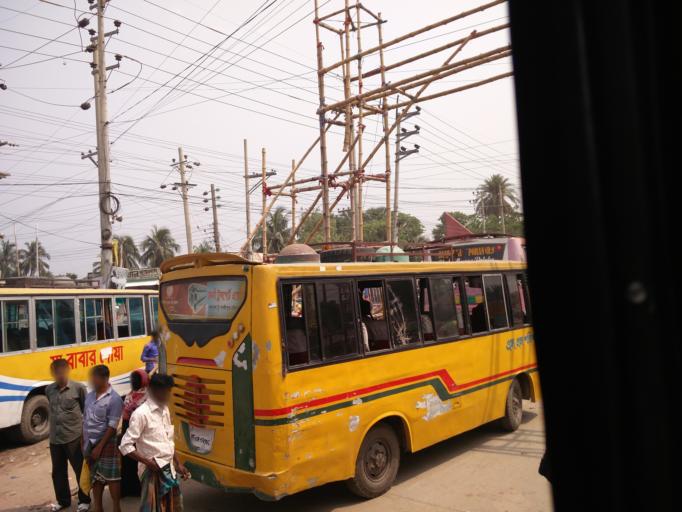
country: BD
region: Dhaka
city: Gafargaon
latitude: 24.4050
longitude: 90.3862
